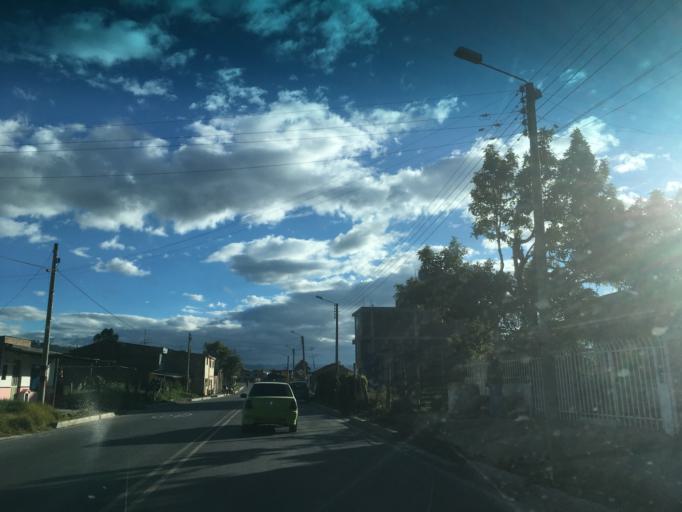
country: CO
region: Boyaca
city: Sogamoso
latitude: 5.7211
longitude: -72.9441
